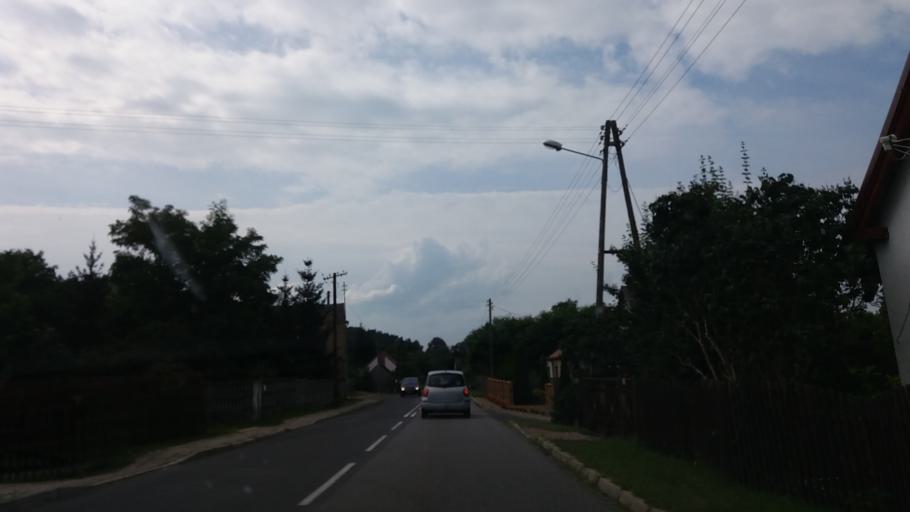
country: PL
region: Lubusz
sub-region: Powiat strzelecko-drezdenecki
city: Zwierzyn
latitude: 52.7242
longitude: 15.5914
